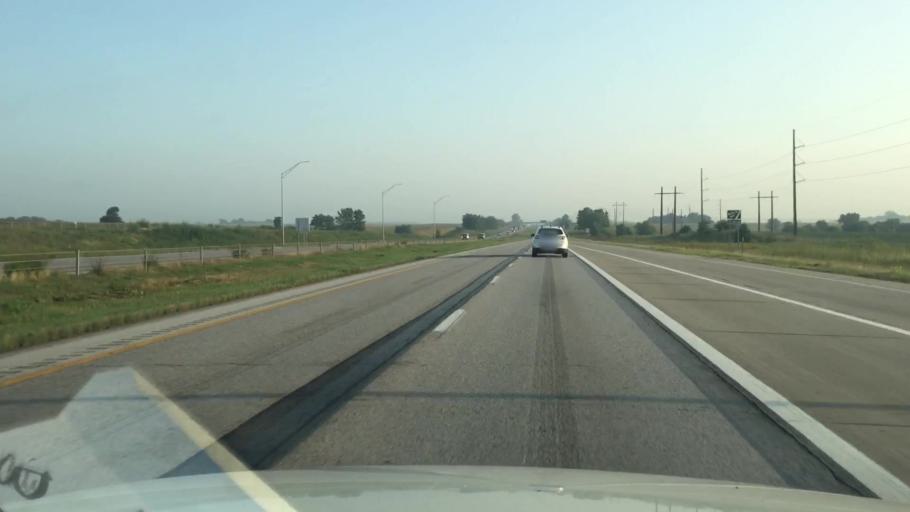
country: US
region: Iowa
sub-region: Story County
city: Huxley
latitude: 41.8365
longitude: -93.5709
